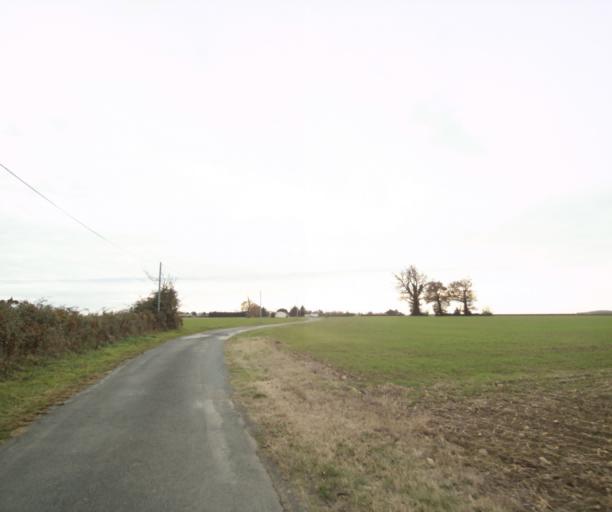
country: FR
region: Poitou-Charentes
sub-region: Departement de la Charente-Maritime
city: Corme-Royal
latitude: 45.7550
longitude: -0.8087
